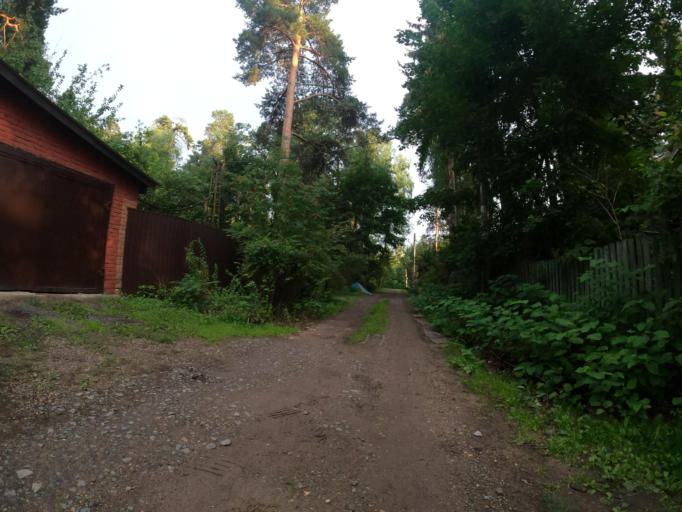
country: RU
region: Moskovskaya
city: Bykovo
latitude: 55.6381
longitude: 38.0962
